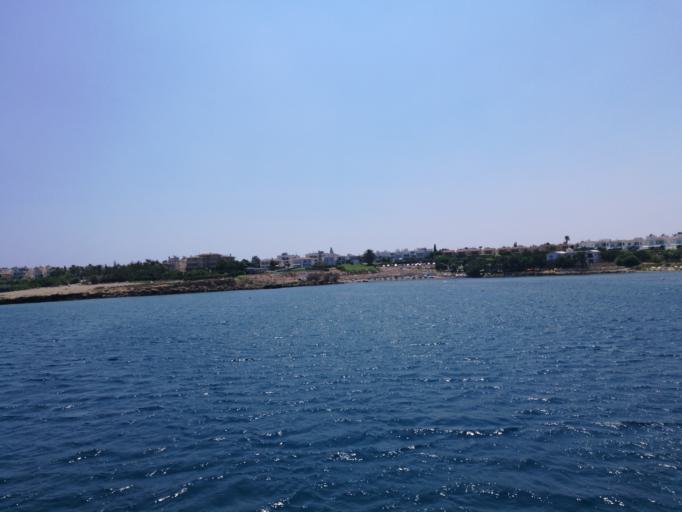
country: CY
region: Ammochostos
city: Protaras
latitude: 35.0422
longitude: 34.0371
